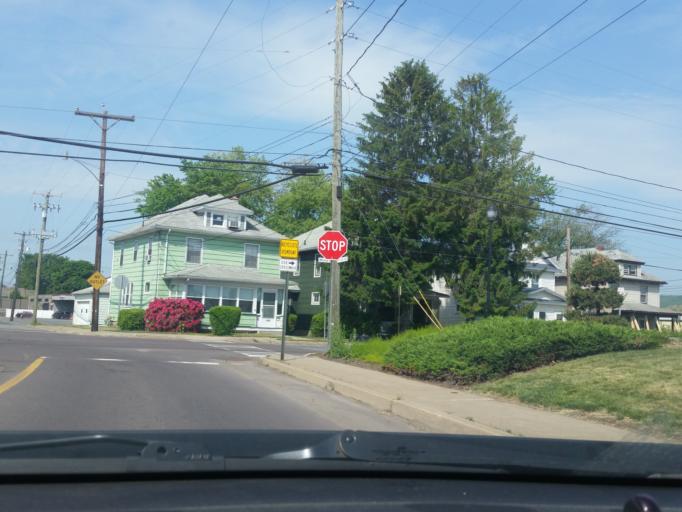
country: US
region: Pennsylvania
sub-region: Luzerne County
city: Forty Fort
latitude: 41.2736
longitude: -75.8742
